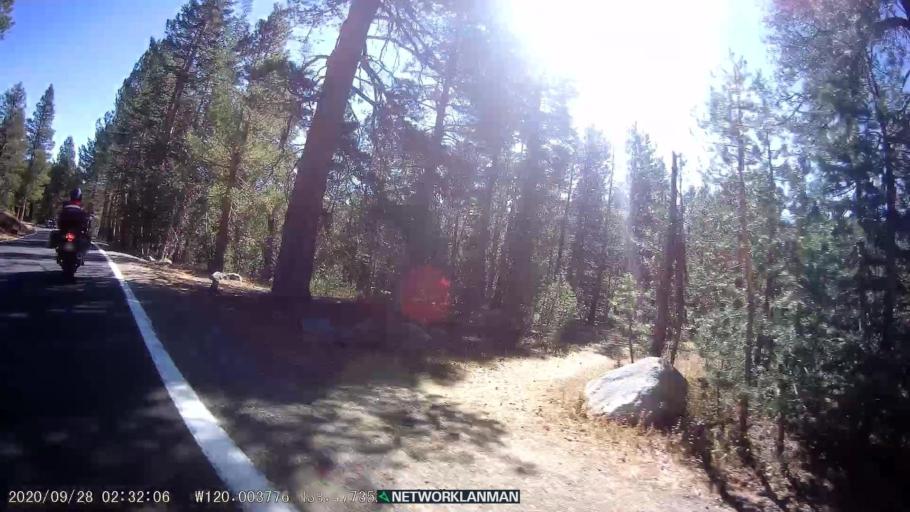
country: US
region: California
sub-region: Calaveras County
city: Arnold
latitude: 38.4775
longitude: -120.0040
